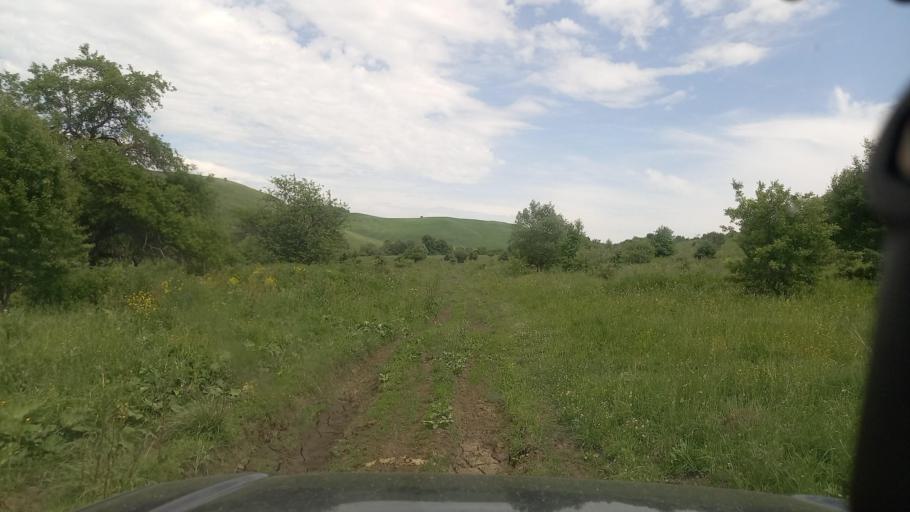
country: RU
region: Karachayevo-Cherkesiya
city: Pregradnaya
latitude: 44.0770
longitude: 41.2695
